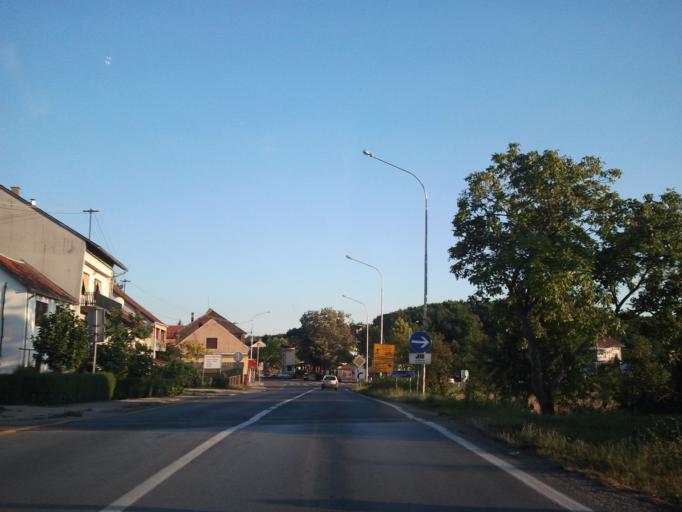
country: HR
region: Sisacko-Moslavacka
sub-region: Grad Sisak
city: Sisak
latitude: 45.4445
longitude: 16.3679
